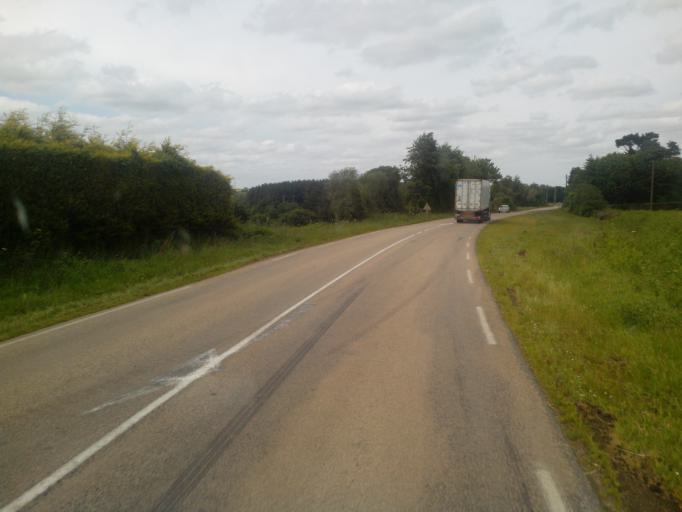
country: FR
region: Brittany
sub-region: Departement du Finistere
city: Guerlesquin
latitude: 48.5308
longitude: -3.5986
